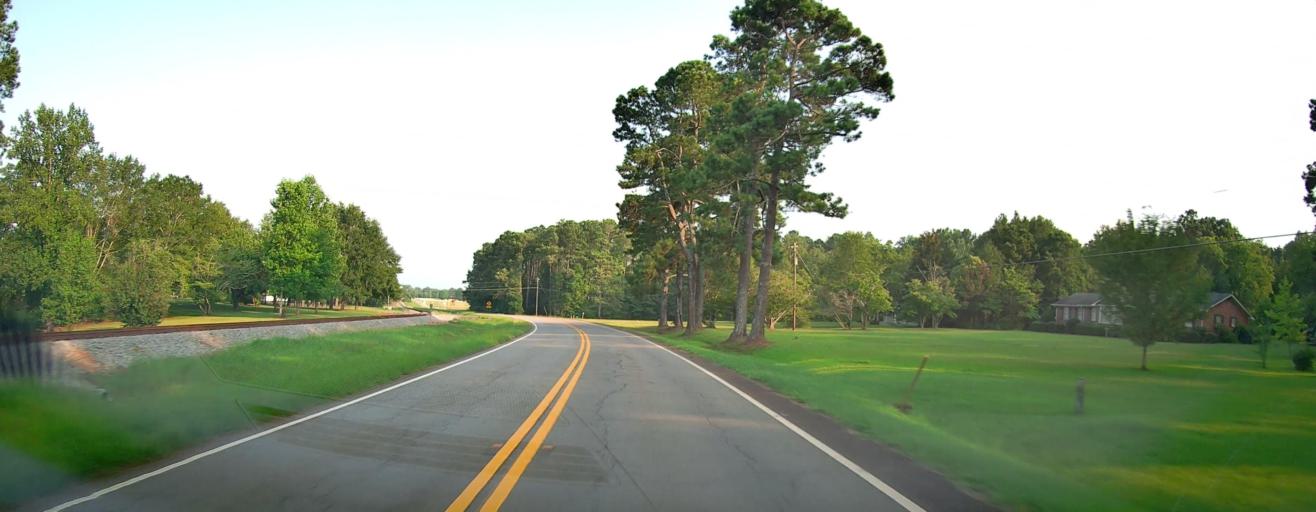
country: US
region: Georgia
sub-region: Jones County
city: Gray
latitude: 33.0489
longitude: -83.5567
